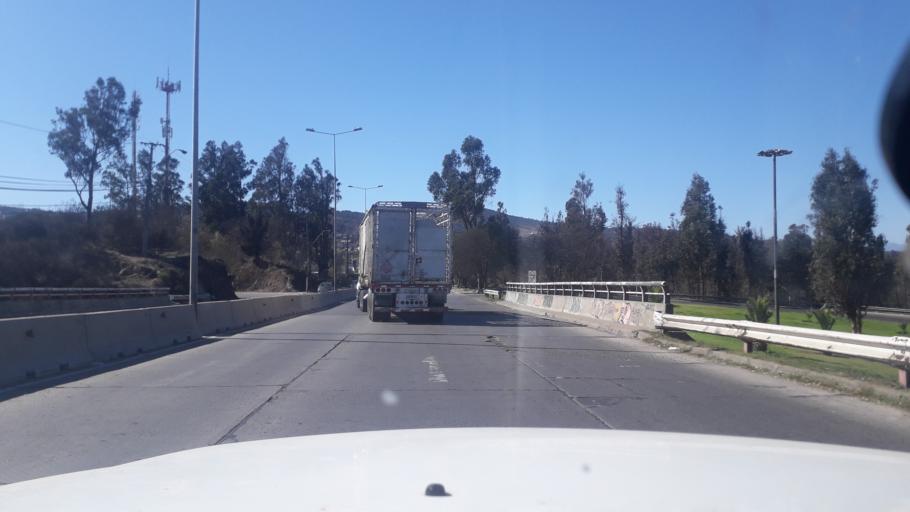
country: CL
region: Valparaiso
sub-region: Provincia de Valparaiso
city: Vina del Mar
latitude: -33.0368
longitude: -71.5015
